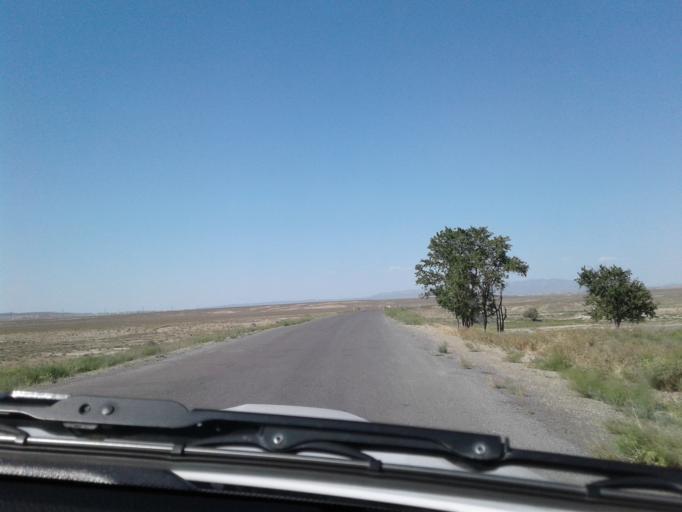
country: TM
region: Balkan
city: Magtymguly
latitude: 38.6004
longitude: 56.1953
